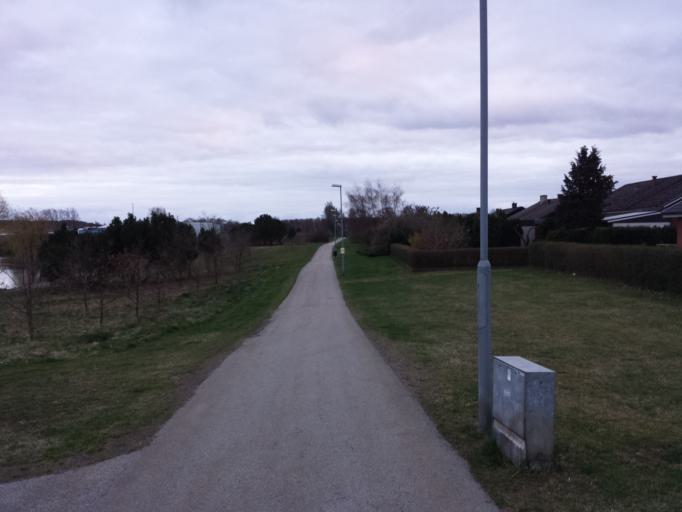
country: SE
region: Skane
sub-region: Sjobo Kommun
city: Sjoebo
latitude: 55.6406
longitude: 13.7000
